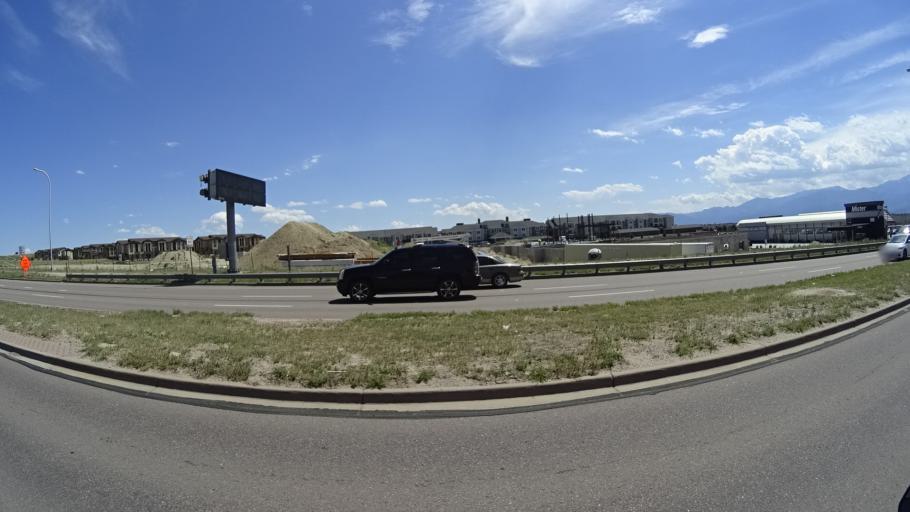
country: US
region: Colorado
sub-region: El Paso County
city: Black Forest
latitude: 38.9403
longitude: -104.7260
